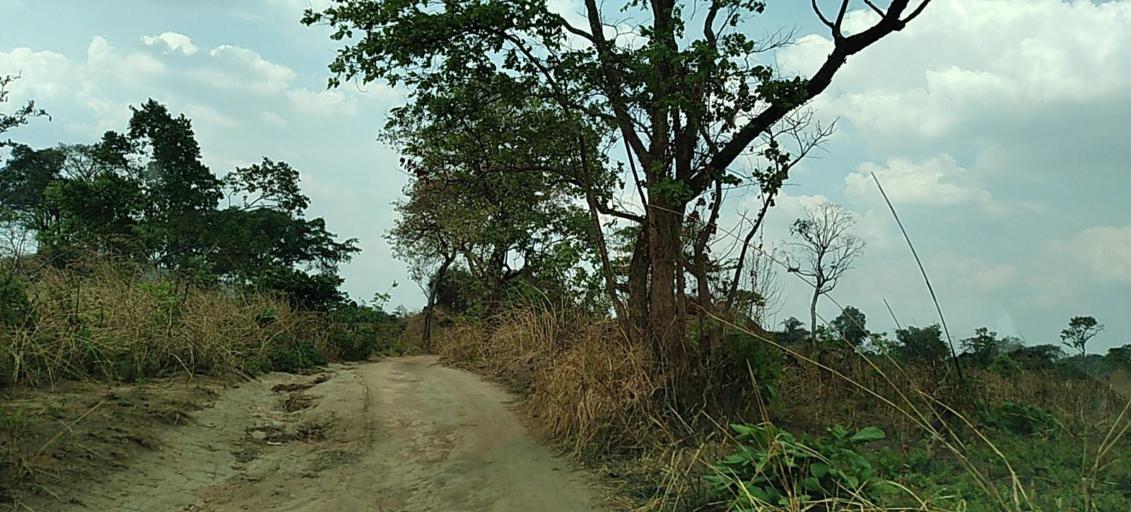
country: ZM
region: Copperbelt
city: Chililabombwe
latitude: -12.3276
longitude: 27.7483
